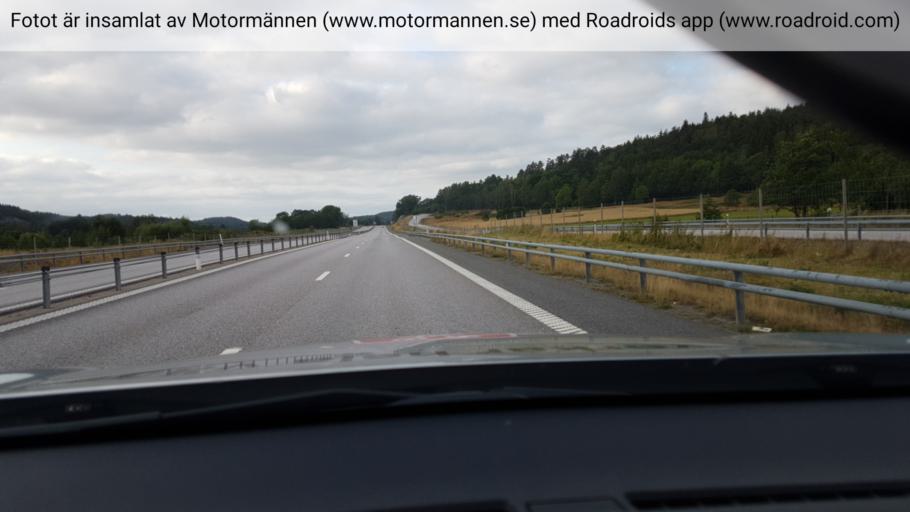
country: SE
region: Vaestra Goetaland
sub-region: Lilla Edets Kommun
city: Lilla Edet
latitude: 58.0878
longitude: 12.1567
